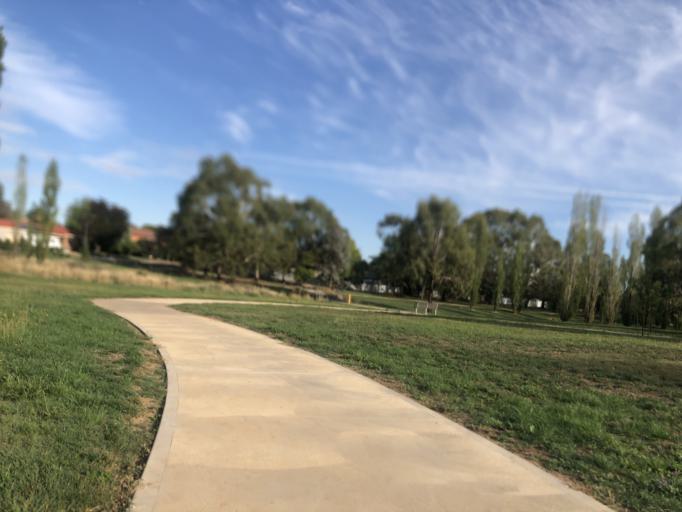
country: AU
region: New South Wales
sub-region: Orange Municipality
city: Orange
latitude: -33.2985
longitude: 149.0922
